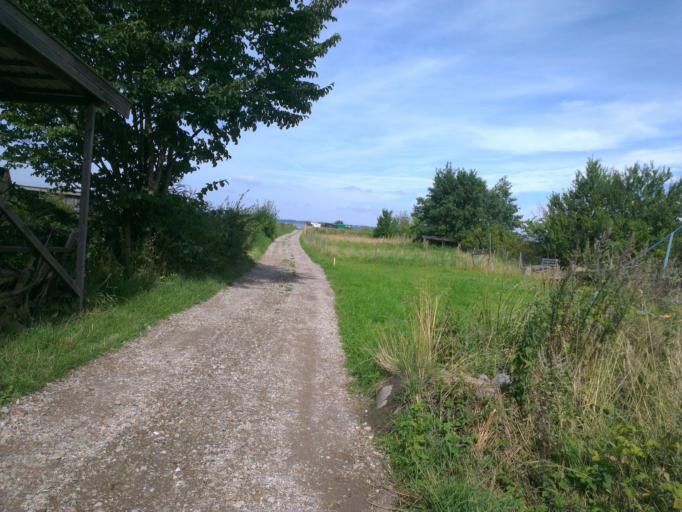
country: DK
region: Capital Region
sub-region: Frederikssund Kommune
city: Jaegerspris
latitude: 55.8567
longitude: 11.9996
